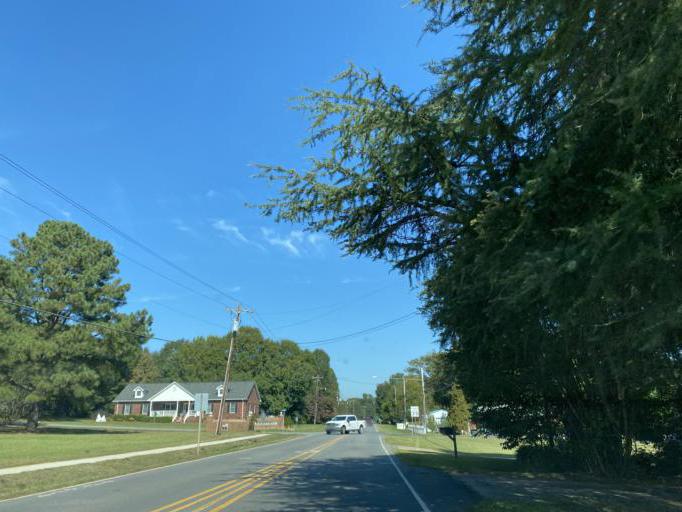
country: US
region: North Carolina
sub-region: Cleveland County
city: Boiling Springs
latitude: 35.2635
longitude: -81.6675
